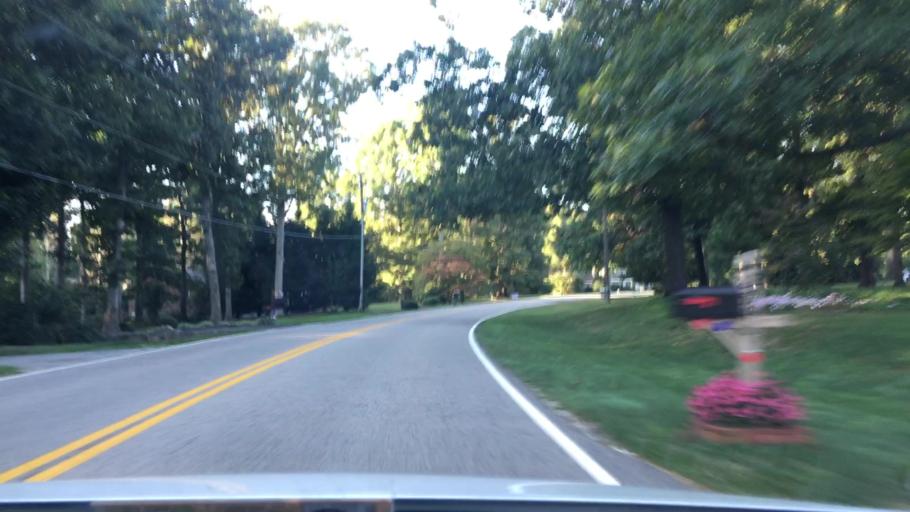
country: US
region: Virginia
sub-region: Chesterfield County
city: Bon Air
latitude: 37.5270
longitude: -77.6414
